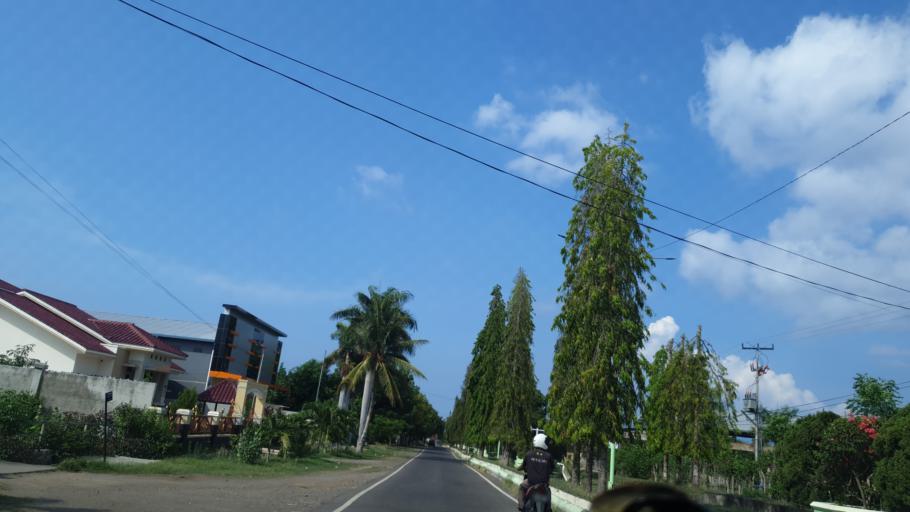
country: ID
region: East Nusa Tenggara
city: Waioti
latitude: -8.6316
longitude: 122.2364
